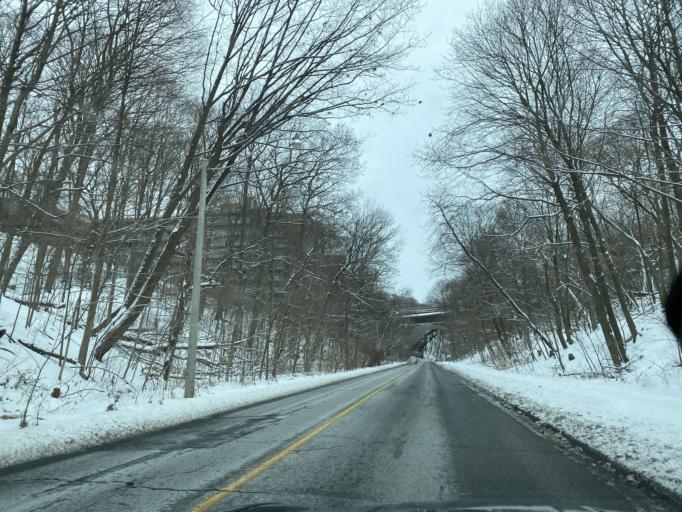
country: CA
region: Ontario
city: Toronto
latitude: 43.6729
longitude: -79.3736
